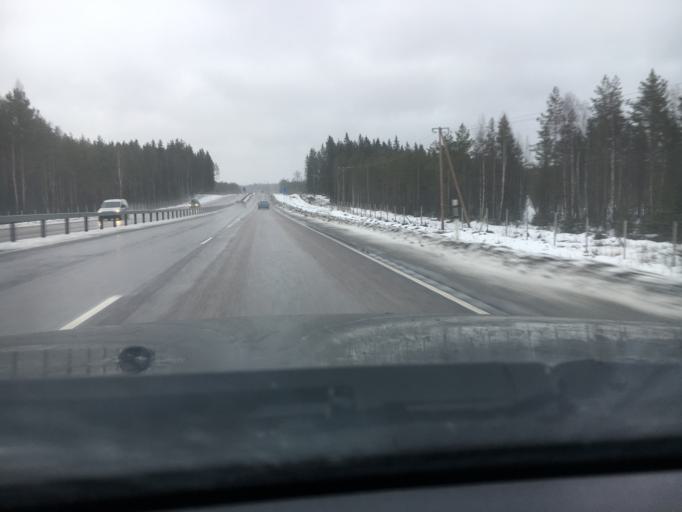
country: FI
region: Central Finland
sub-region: Joutsa
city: Joutsa
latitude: 61.8143
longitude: 26.0937
